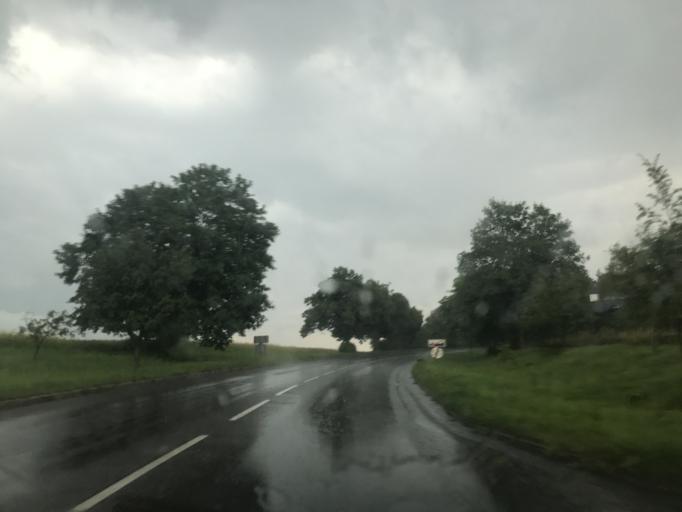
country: PL
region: Pomeranian Voivodeship
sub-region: Powiat chojnicki
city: Chojnice
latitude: 53.7032
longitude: 17.5987
